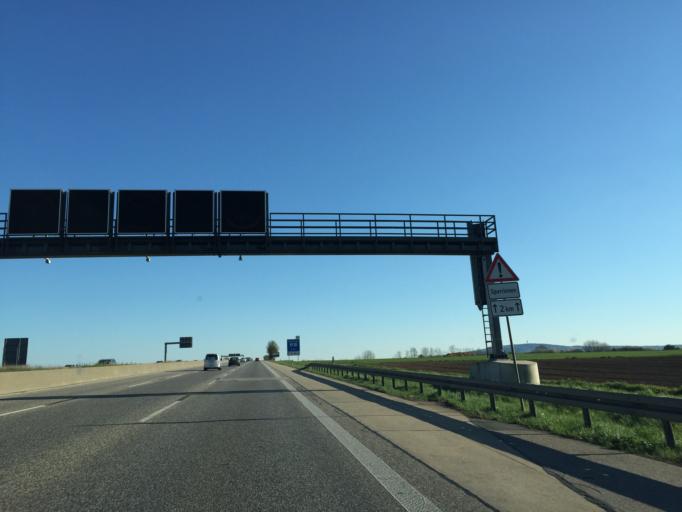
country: DE
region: Hesse
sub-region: Regierungsbezirk Darmstadt
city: Ober-Morlen
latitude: 50.4026
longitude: 8.7010
